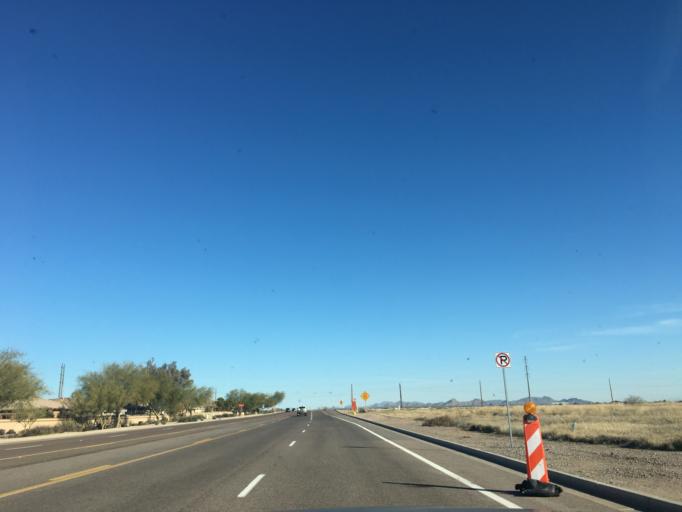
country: US
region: Arizona
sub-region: Pinal County
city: Maricopa
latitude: 33.0436
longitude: -112.0004
